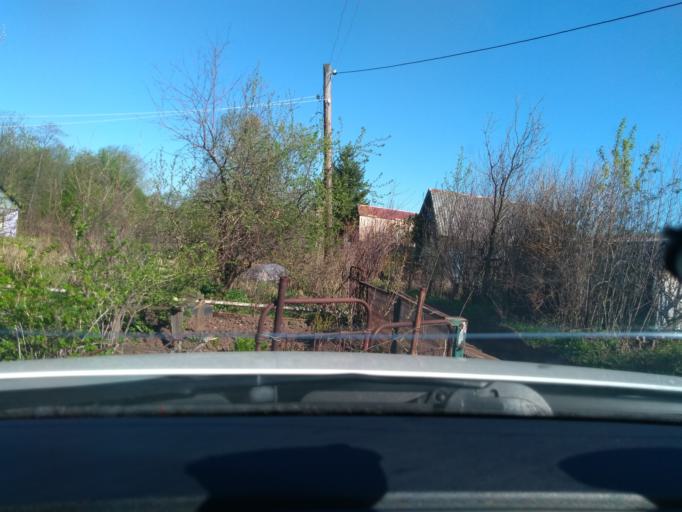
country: RU
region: Perm
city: Lobanovo
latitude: 57.8708
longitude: 56.3035
